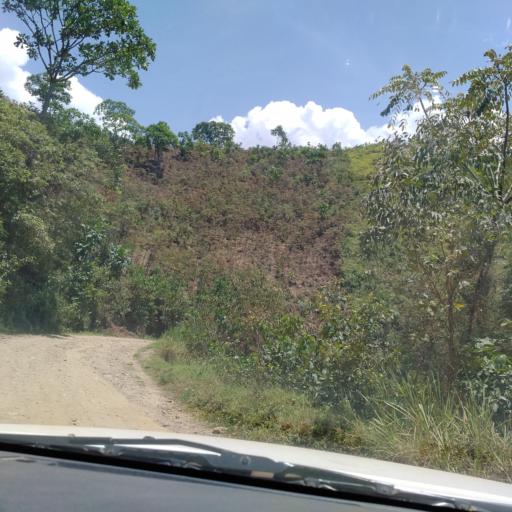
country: CD
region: Nord Kivu
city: Sake
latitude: -1.9511
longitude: 28.9276
